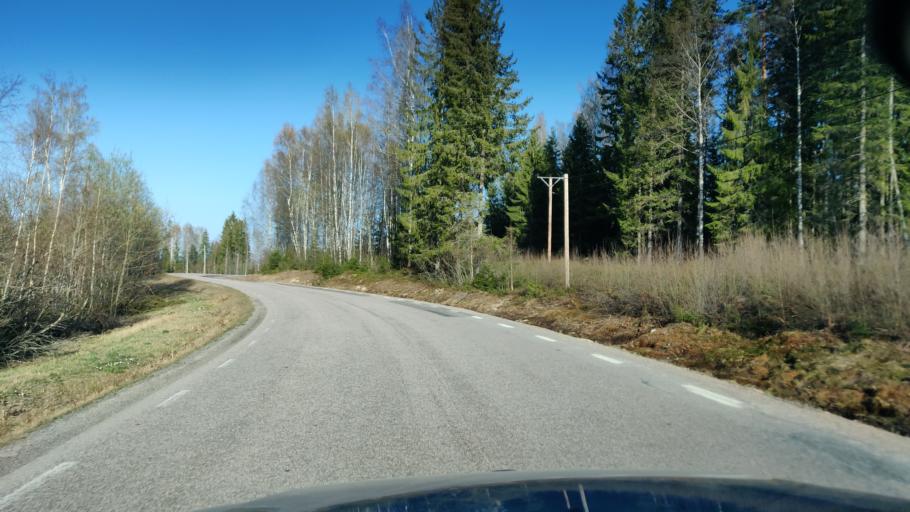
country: SE
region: Vaermland
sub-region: Munkfors Kommun
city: Munkfors
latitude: 59.9703
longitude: 13.4507
